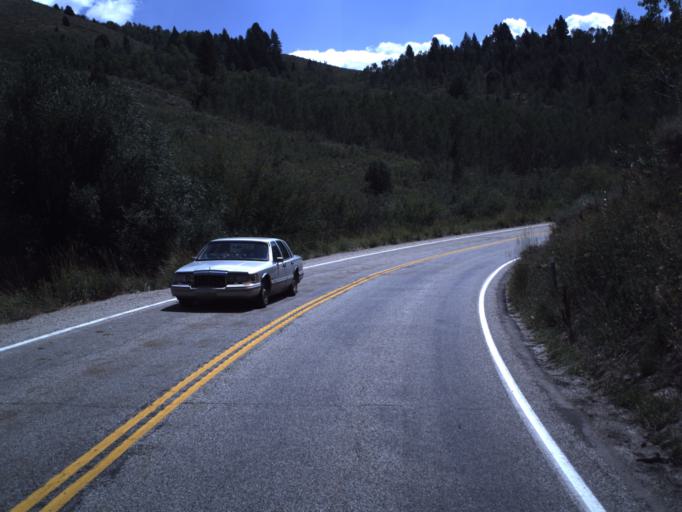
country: US
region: Utah
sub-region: Cache County
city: North Logan
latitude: 41.8512
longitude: -111.5846
